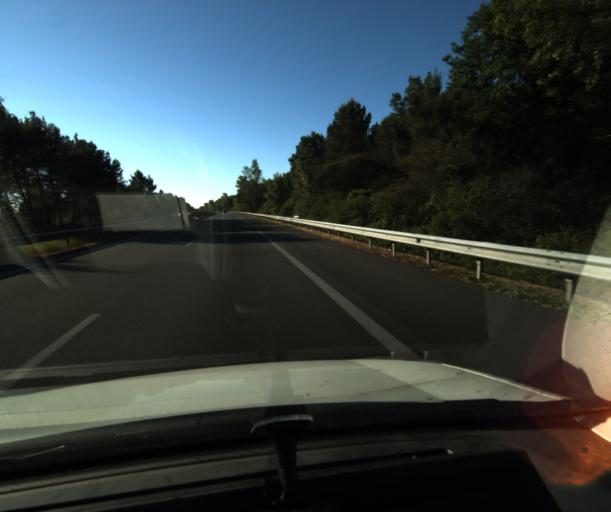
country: FR
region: Midi-Pyrenees
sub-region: Departement du Tarn-et-Garonne
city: Montech
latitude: 43.9676
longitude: 1.2705
